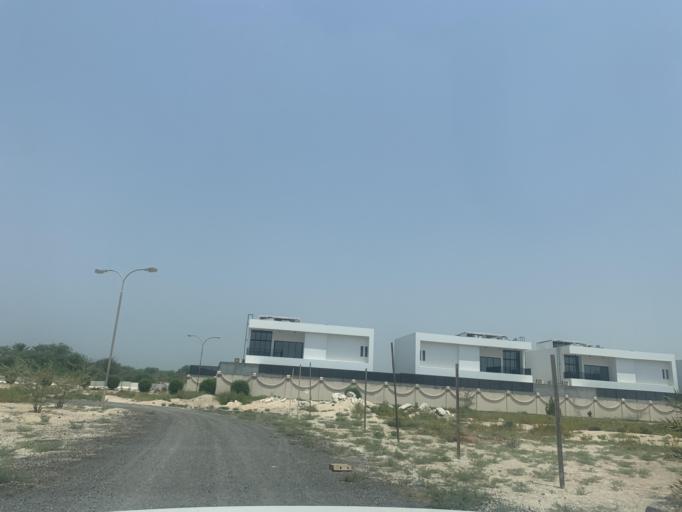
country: BH
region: Central Governorate
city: Madinat Hamad
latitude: 26.1469
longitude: 50.4592
